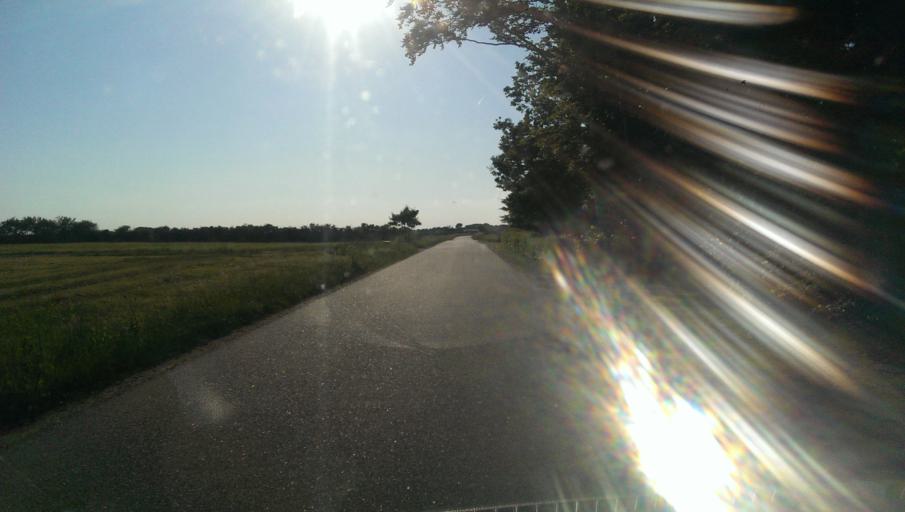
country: DK
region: South Denmark
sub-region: Esbjerg Kommune
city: Bramming
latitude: 55.5663
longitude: 8.6849
